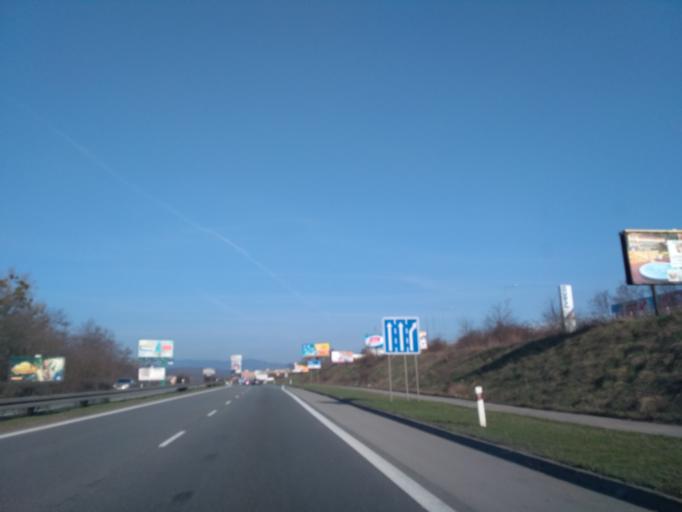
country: SK
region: Kosicky
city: Kosice
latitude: 48.6904
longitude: 21.2446
